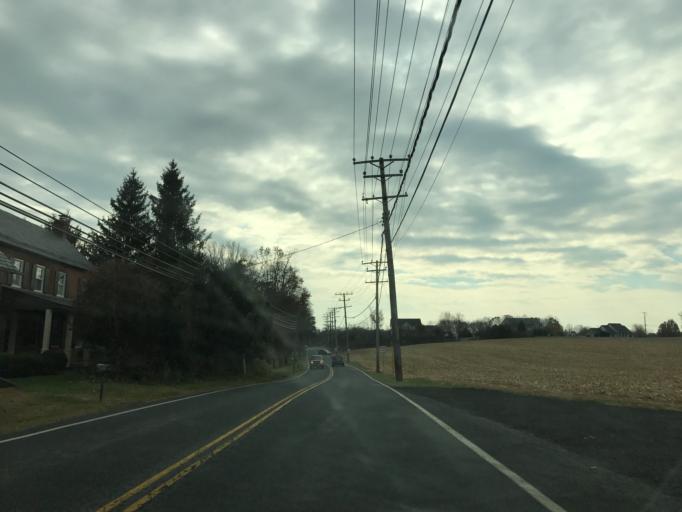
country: US
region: Maryland
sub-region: Harford County
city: Jarrettsville
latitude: 39.5966
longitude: -76.4401
